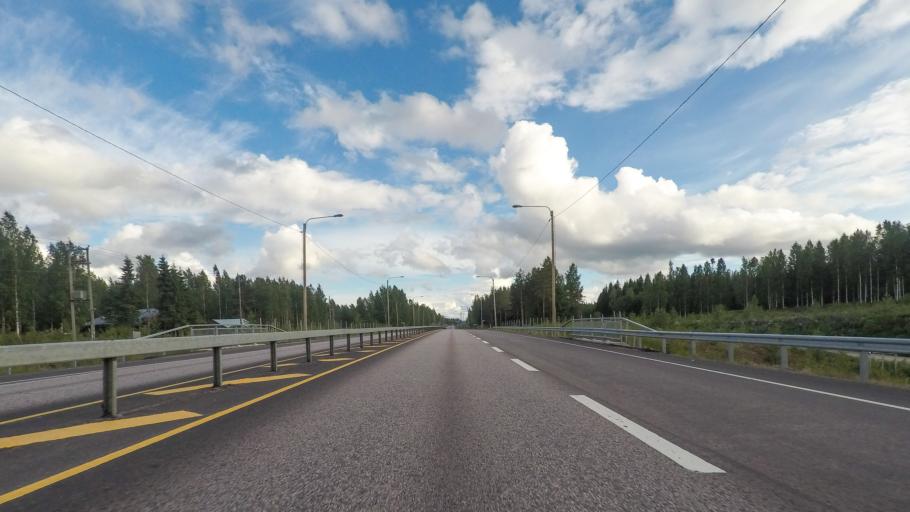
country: FI
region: Central Finland
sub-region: Joutsa
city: Joutsa
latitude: 61.7958
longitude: 26.0941
